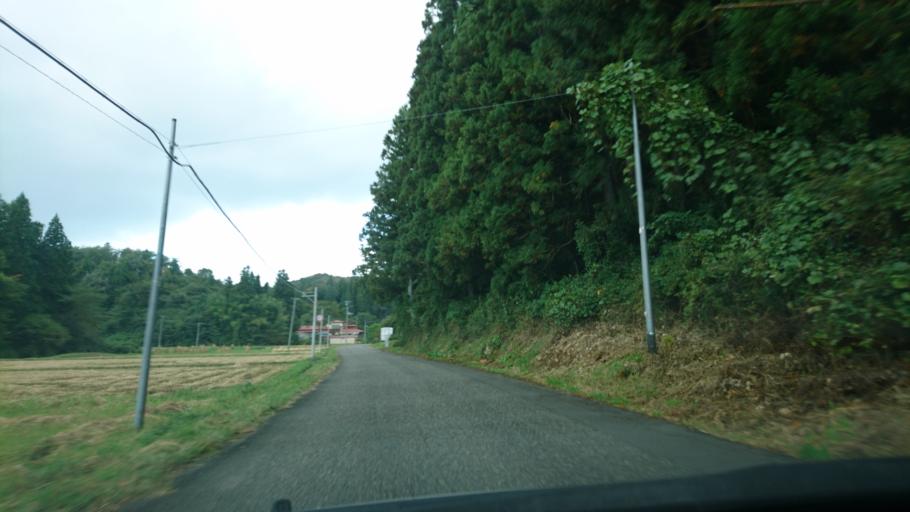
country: JP
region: Iwate
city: Ichinoseki
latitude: 38.9014
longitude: 141.0835
